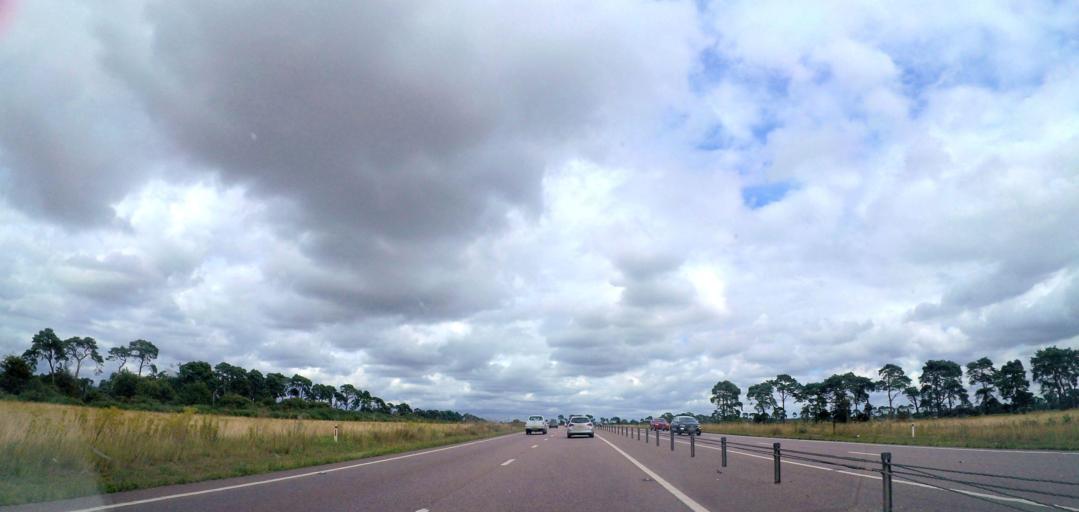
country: GB
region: England
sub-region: Suffolk
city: Lakenheath
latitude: 52.3569
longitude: 0.5892
